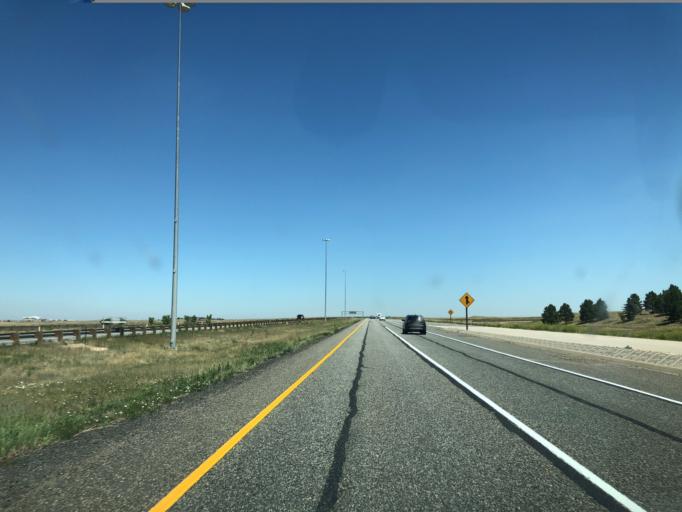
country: US
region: Colorado
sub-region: Adams County
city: Aurora
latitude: 39.7716
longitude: -104.7164
